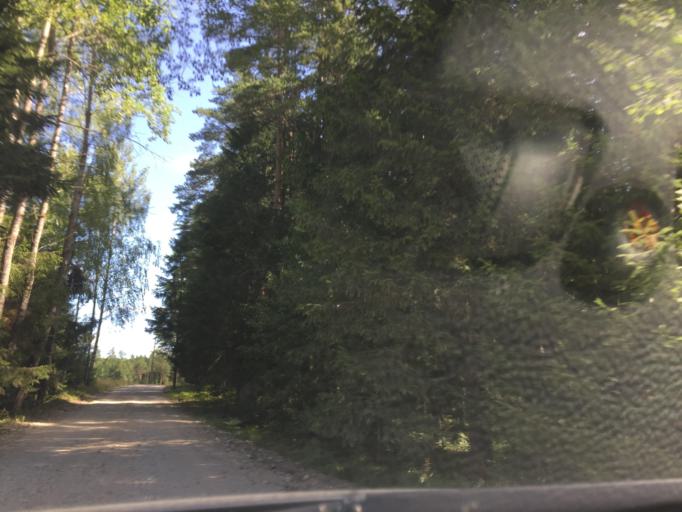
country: LV
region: Talsu Rajons
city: Stende
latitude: 57.1909
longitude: 22.3281
